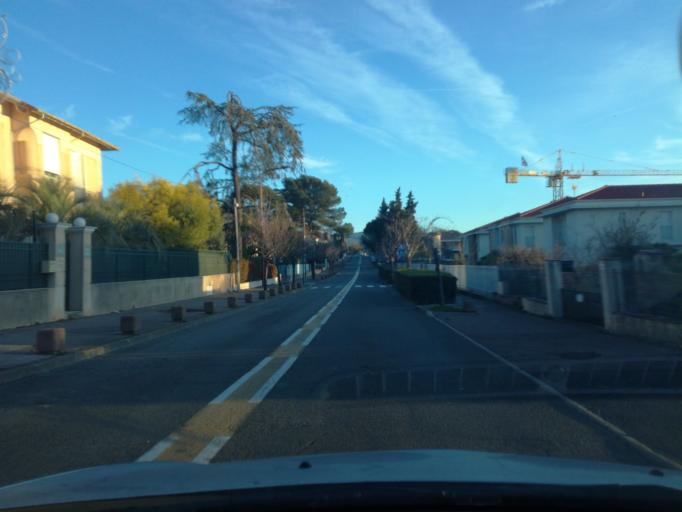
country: FR
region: Provence-Alpes-Cote d'Azur
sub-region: Departement du Var
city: Frejus
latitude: 43.4354
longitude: 6.7390
